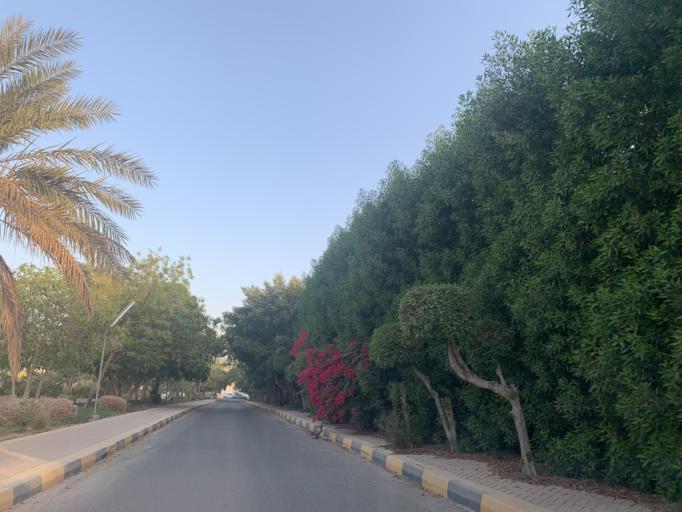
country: BH
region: Manama
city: Jidd Hafs
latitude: 26.2206
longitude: 50.5306
